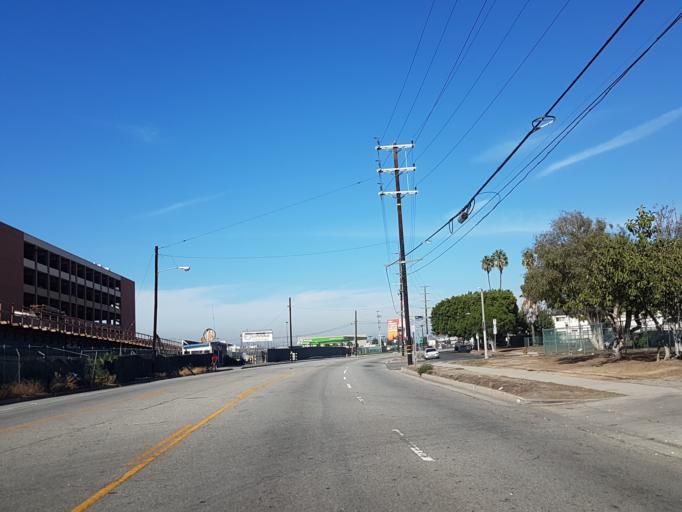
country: US
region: California
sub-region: Los Angeles County
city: Lennox
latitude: 33.9473
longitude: -118.3784
